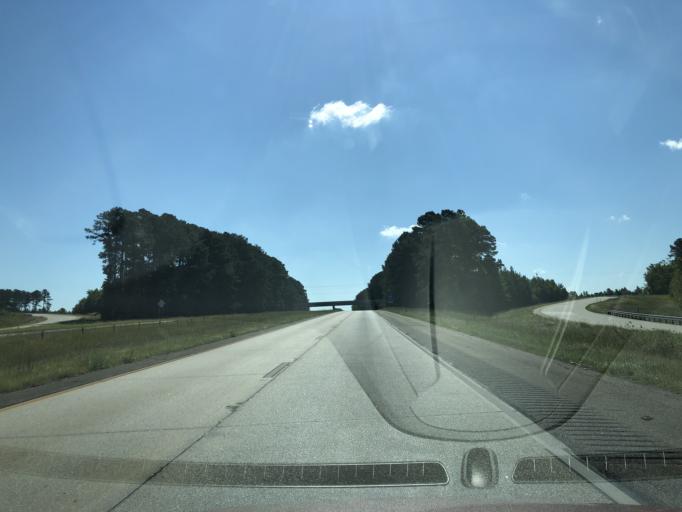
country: US
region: Georgia
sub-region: McDuffie County
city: Thomson
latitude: 33.5051
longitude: -82.5591
